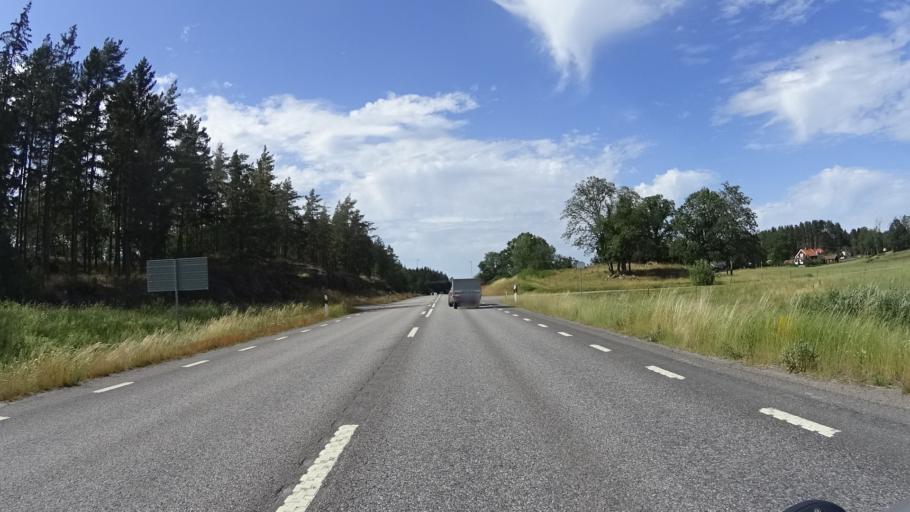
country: SE
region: OEstergoetland
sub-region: Linkopings Kommun
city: Linghem
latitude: 58.3543
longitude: 15.8333
